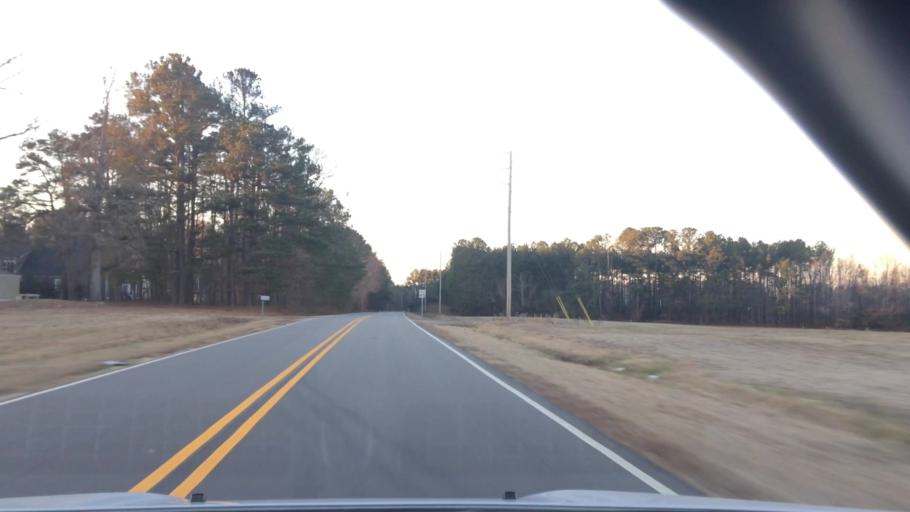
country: US
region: North Carolina
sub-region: Wake County
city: Rolesville
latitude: 35.9464
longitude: -78.4074
